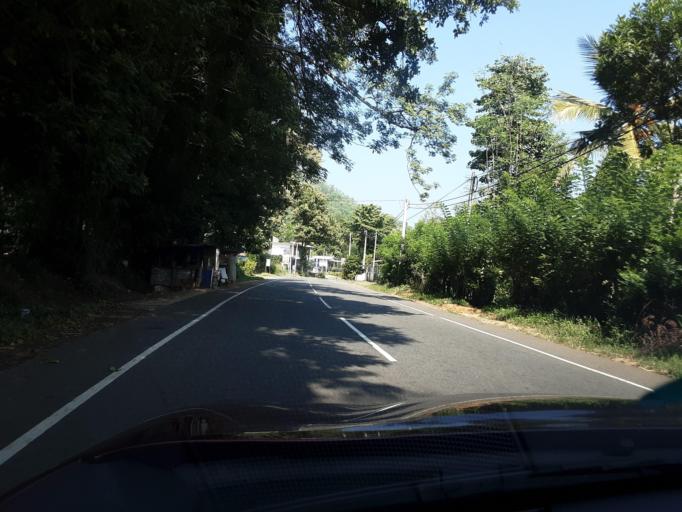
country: LK
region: Uva
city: Badulla
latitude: 7.1672
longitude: 81.0518
